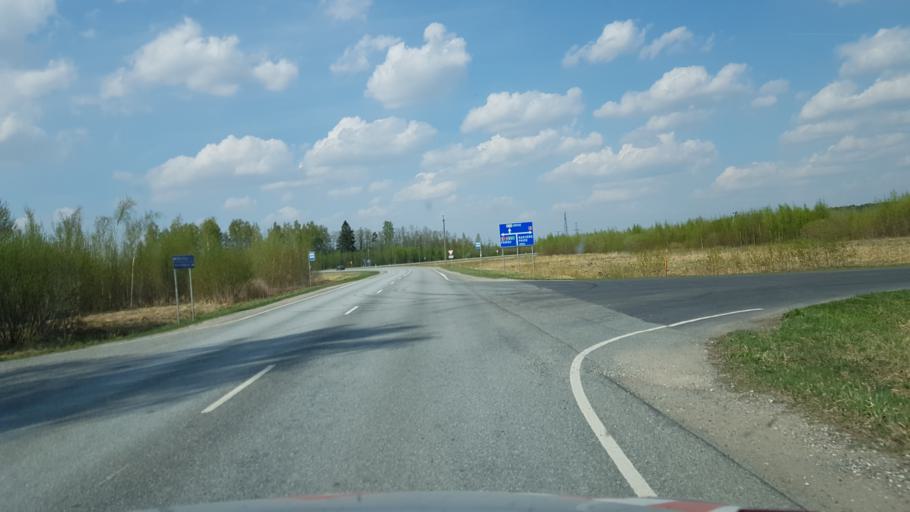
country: EE
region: Paernumaa
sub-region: Sindi linn
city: Sindi
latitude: 58.4202
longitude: 24.6702
